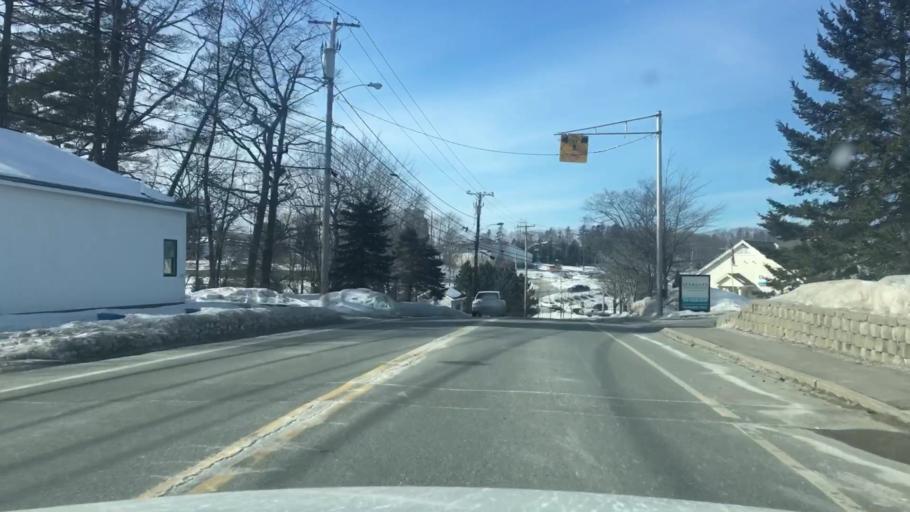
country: US
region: Maine
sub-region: Hancock County
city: Bucksport
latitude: 44.5756
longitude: -68.8020
